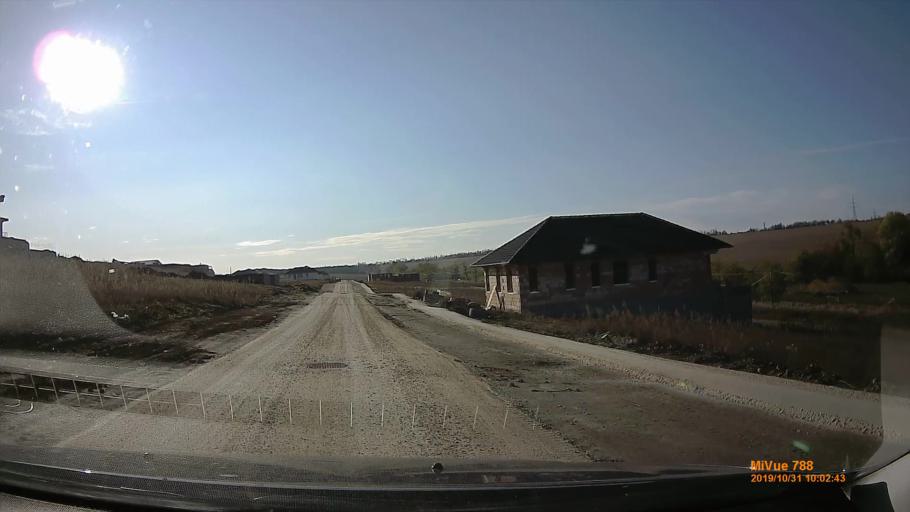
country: HU
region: Pest
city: Pecel
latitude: 47.4715
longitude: 19.3441
